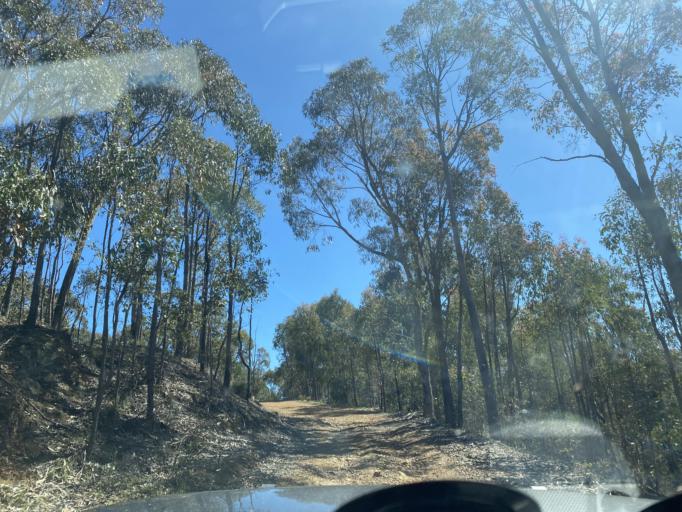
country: AU
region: Victoria
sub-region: Benalla
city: Benalla
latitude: -36.7292
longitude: 146.1817
